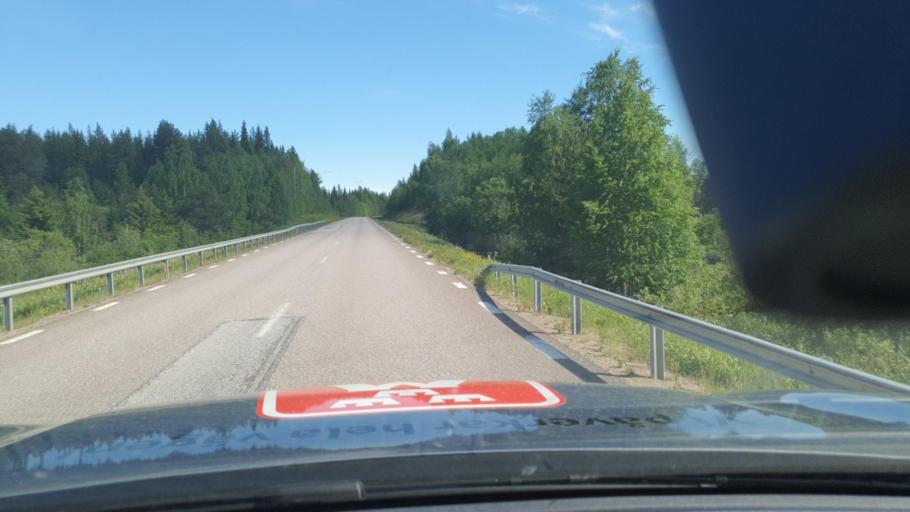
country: SE
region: Norrbotten
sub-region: Overkalix Kommun
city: OEverkalix
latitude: 66.7750
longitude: 22.6944
